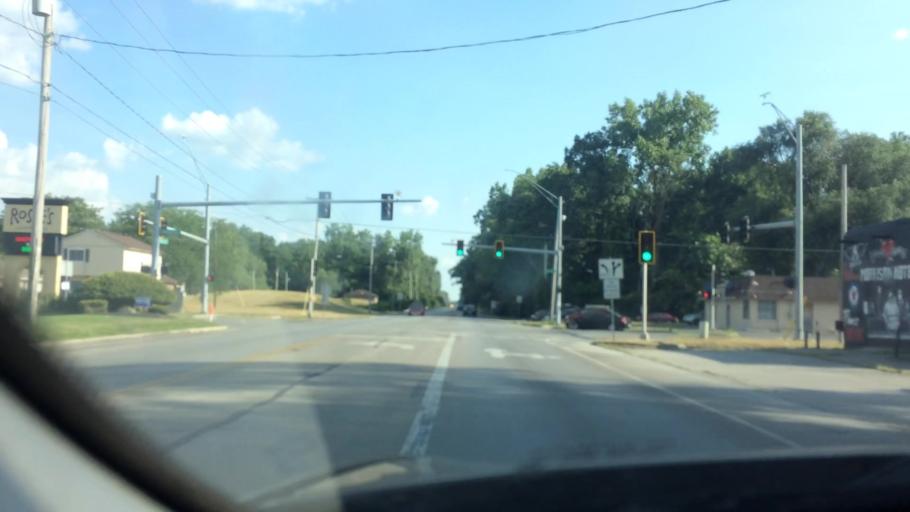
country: US
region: Ohio
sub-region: Lucas County
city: Holland
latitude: 41.6472
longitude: -83.7036
